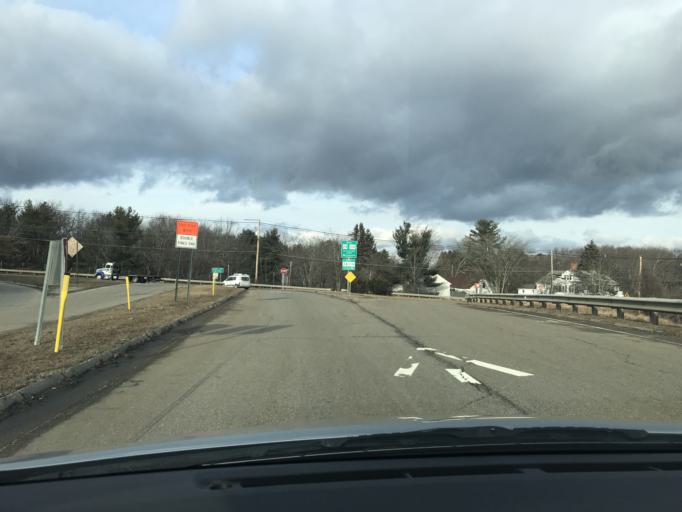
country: US
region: Massachusetts
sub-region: Middlesex County
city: Littleton Common
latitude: 42.5387
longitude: -71.4913
